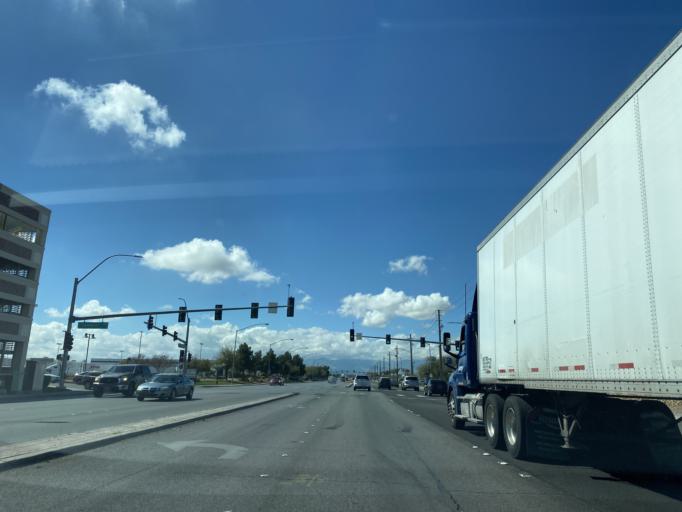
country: US
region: Nevada
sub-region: Clark County
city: North Las Vegas
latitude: 36.2398
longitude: -115.1202
